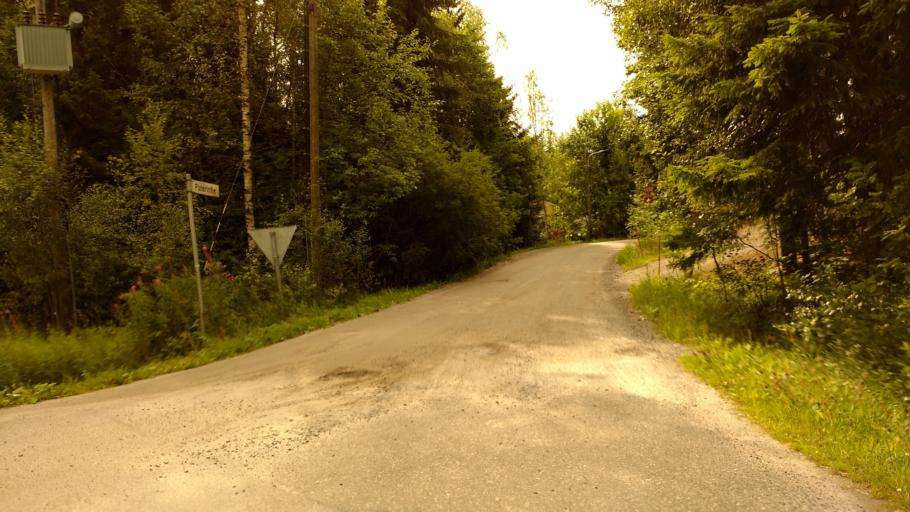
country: FI
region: Varsinais-Suomi
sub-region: Turku
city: Kaarina
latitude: 60.4458
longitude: 22.4214
